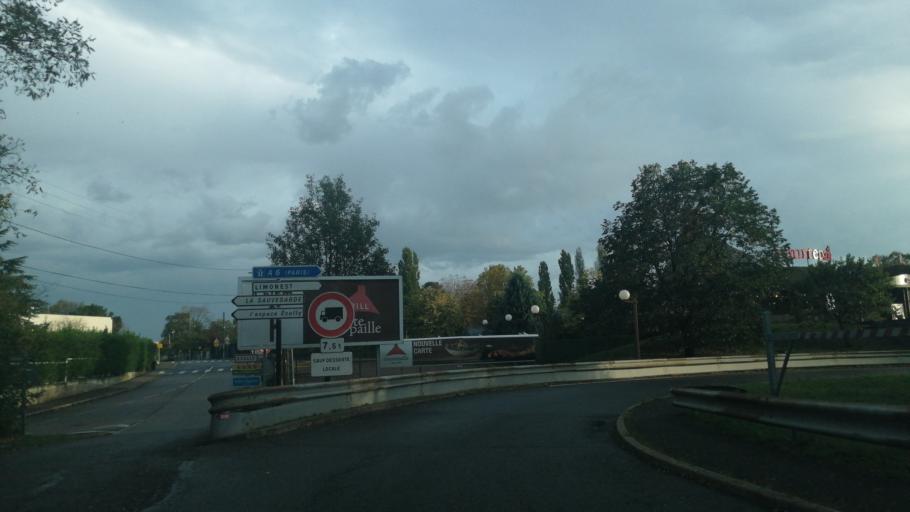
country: FR
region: Rhone-Alpes
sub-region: Departement du Rhone
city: Ecully
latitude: 45.7849
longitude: 4.7860
